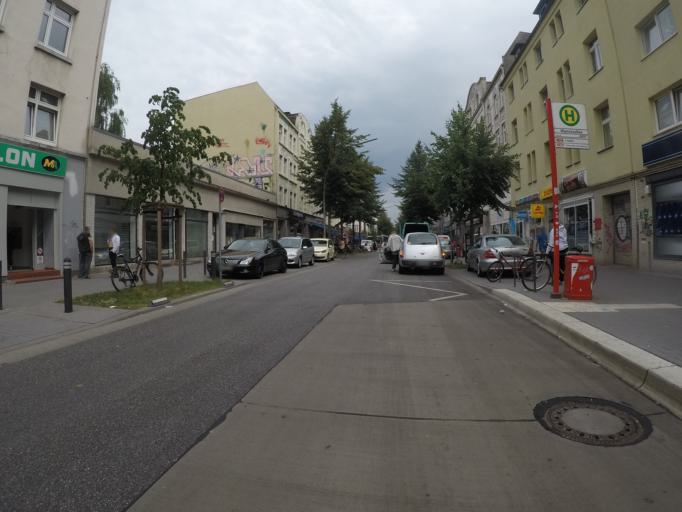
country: DE
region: Hamburg
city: Kleiner Grasbrook
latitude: 53.5147
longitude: 9.9872
